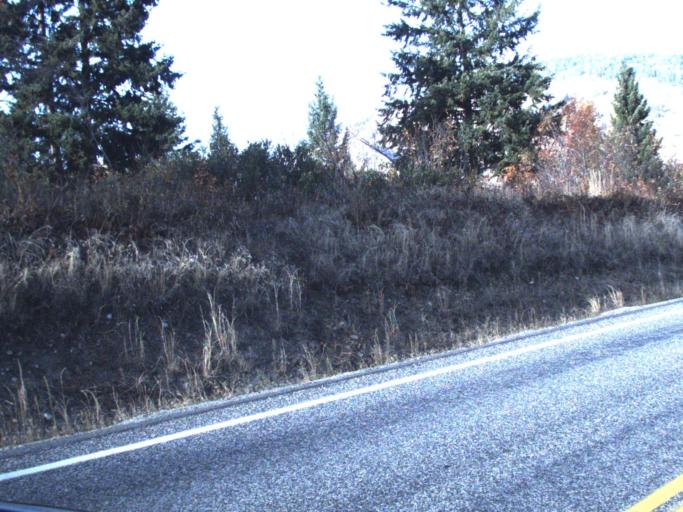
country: CA
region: British Columbia
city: Rossland
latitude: 48.8607
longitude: -117.8769
